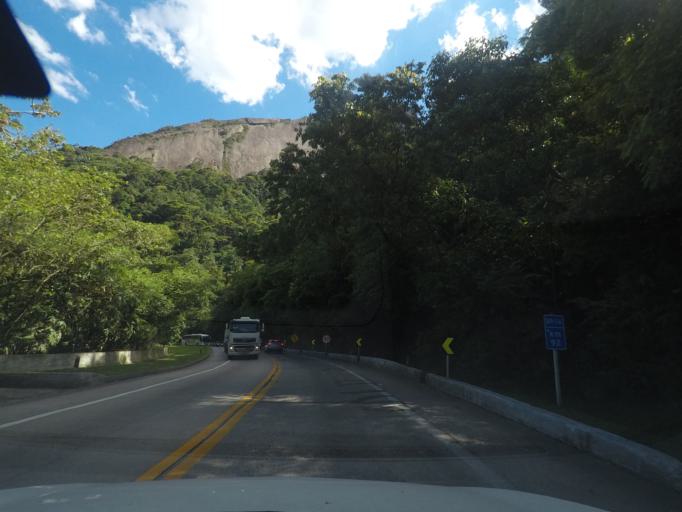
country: BR
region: Rio de Janeiro
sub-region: Teresopolis
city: Teresopolis
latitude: -22.4731
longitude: -43.0013
